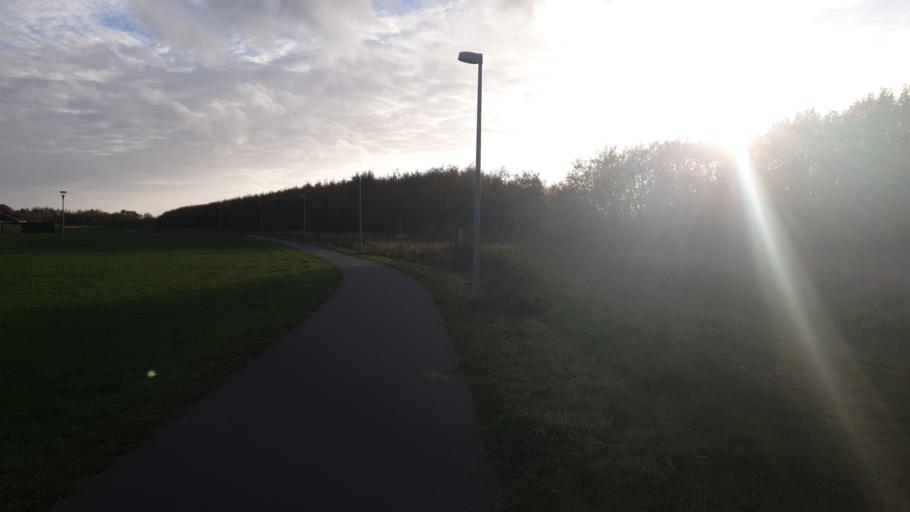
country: DK
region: Central Jutland
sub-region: Hedensted Kommune
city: Hedensted
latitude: 55.7878
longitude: 9.6921
